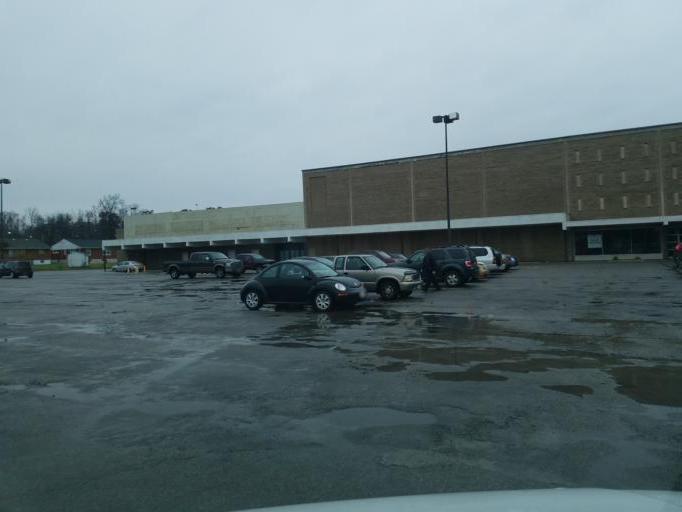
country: US
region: Ohio
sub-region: Richland County
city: Ontario
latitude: 40.7601
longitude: -82.5621
